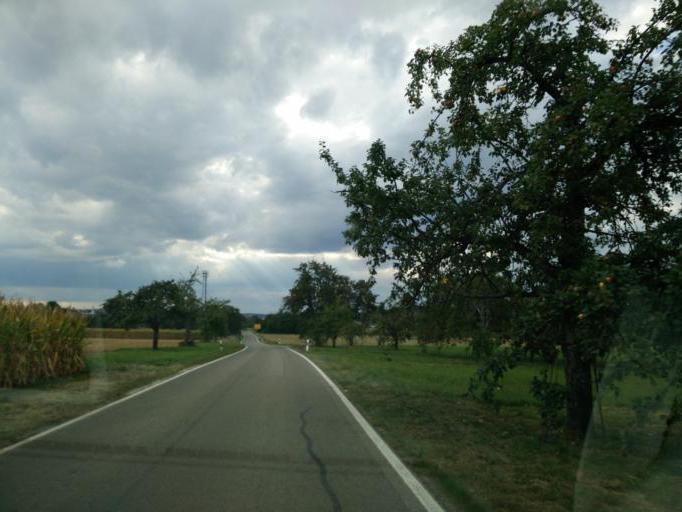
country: DE
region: Baden-Wuerttemberg
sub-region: Tuebingen Region
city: Sickenhausen
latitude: 48.5345
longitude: 9.1663
